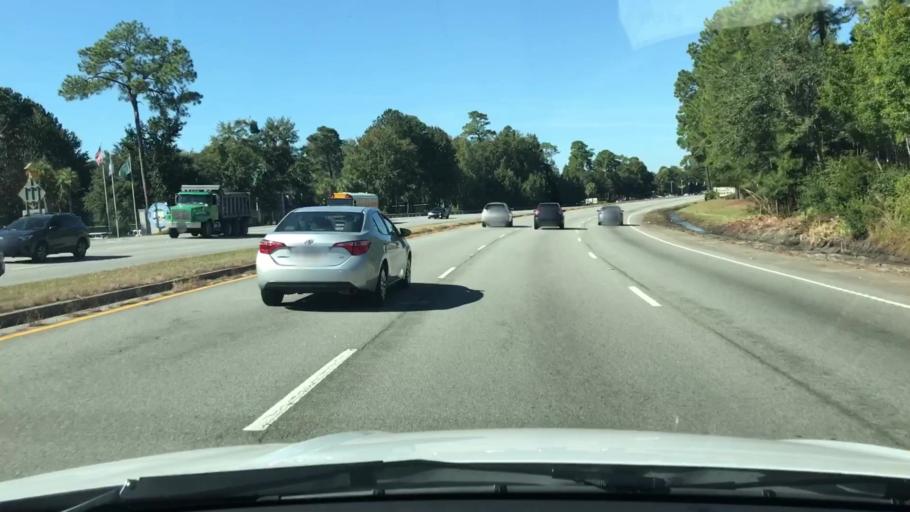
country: US
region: South Carolina
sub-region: Beaufort County
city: Bluffton
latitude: 32.2523
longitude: -80.8445
